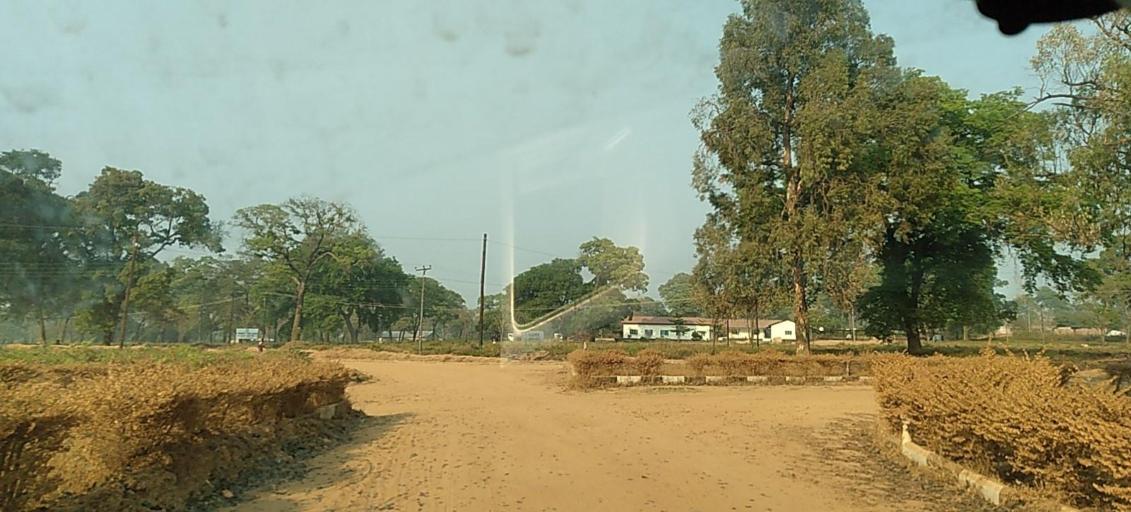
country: ZM
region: North-Western
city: Kabompo
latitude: -13.5987
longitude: 24.2082
